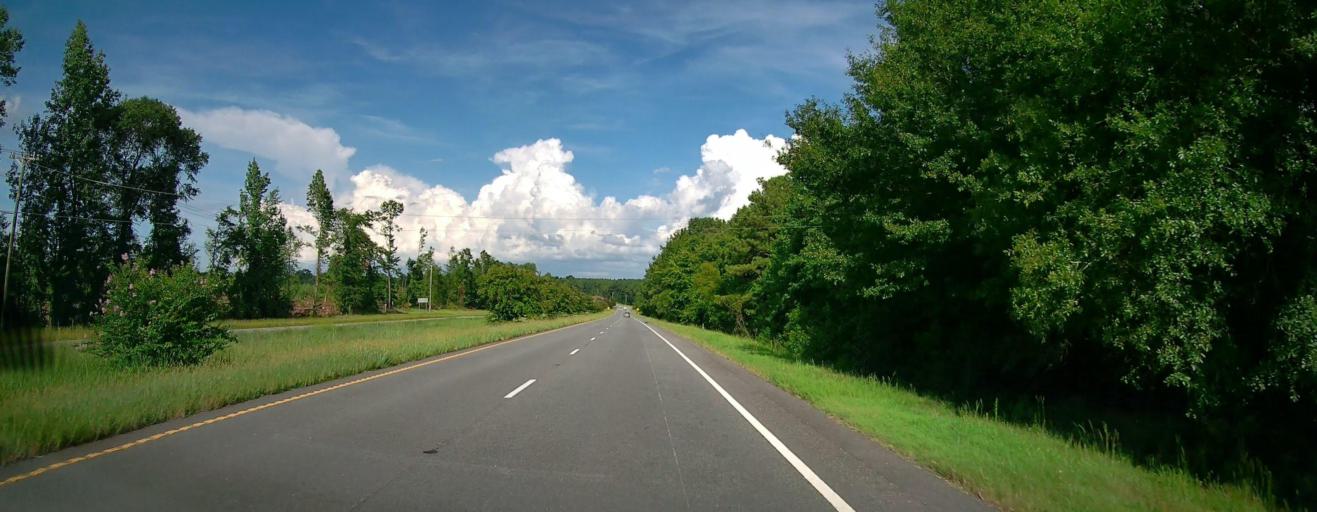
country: US
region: Georgia
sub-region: Talbot County
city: Talbotton
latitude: 32.5457
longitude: -84.7209
